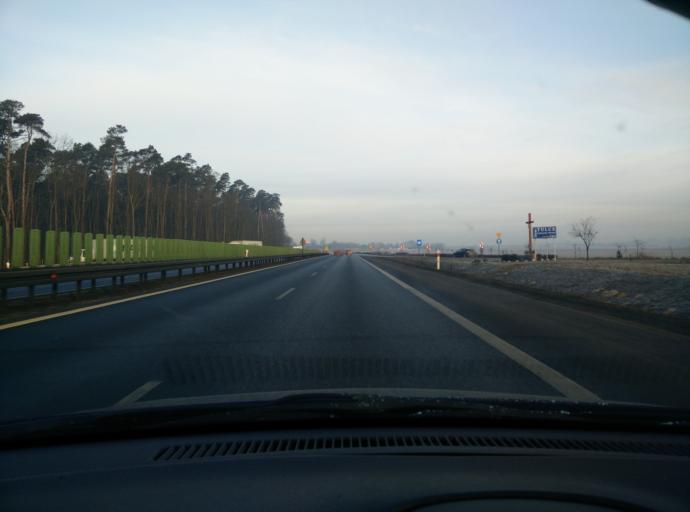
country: PL
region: Greater Poland Voivodeship
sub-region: Powiat poznanski
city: Daszewice
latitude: 52.3247
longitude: 17.0319
